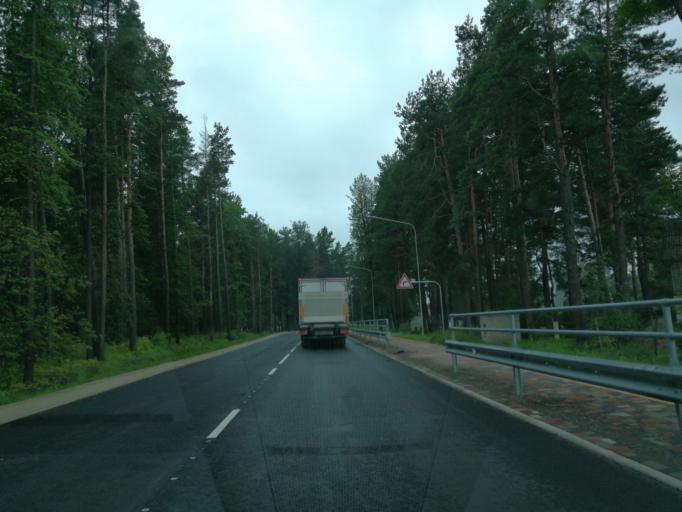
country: LV
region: Livani
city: Livani
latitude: 56.3548
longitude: 26.1840
